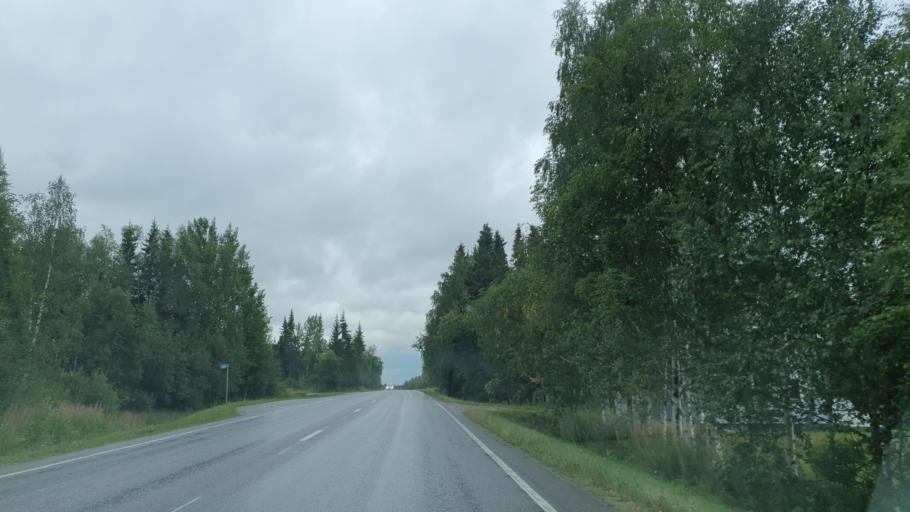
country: FI
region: Lapland
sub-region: Tunturi-Lappi
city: Kolari
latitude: 67.2298
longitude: 23.8932
